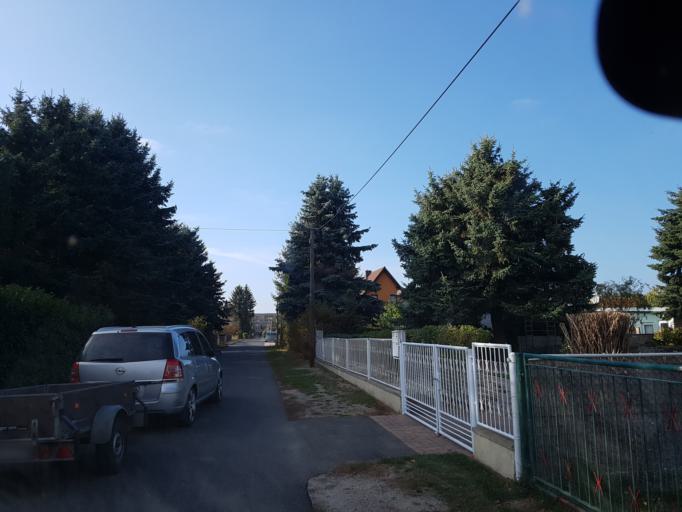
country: DE
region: Brandenburg
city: Finsterwalde
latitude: 51.6208
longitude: 13.7191
